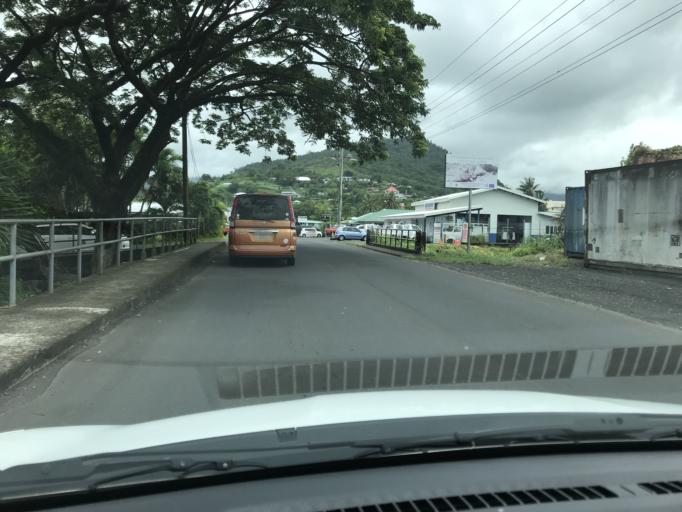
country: WS
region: Tuamasaga
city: Apia
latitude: -13.8341
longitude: -171.7681
